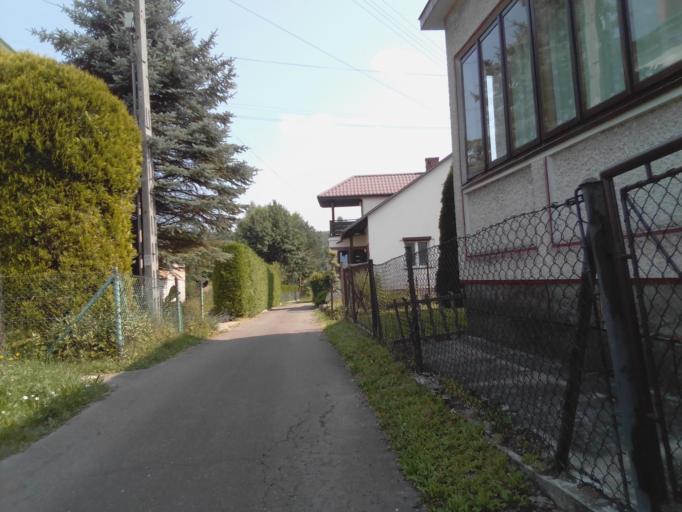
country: PL
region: Subcarpathian Voivodeship
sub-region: Powiat brzozowski
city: Domaradz
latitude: 49.7899
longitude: 21.9470
